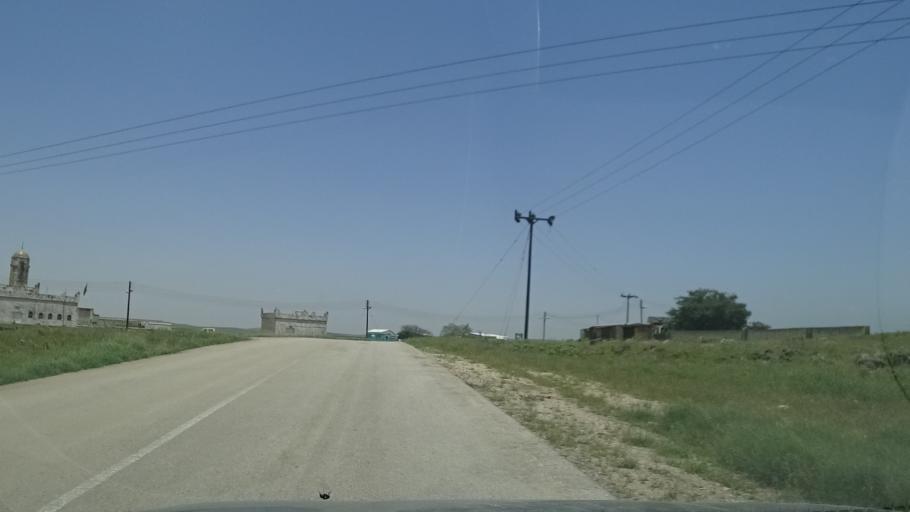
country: OM
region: Zufar
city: Salalah
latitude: 17.2486
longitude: 54.2639
